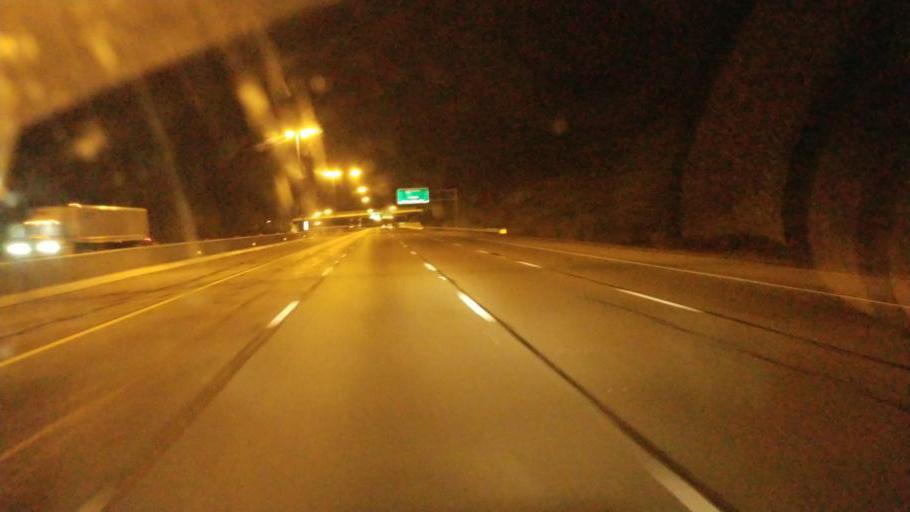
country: US
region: Ohio
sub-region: Montgomery County
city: Vandalia
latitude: 39.8663
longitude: -84.1747
